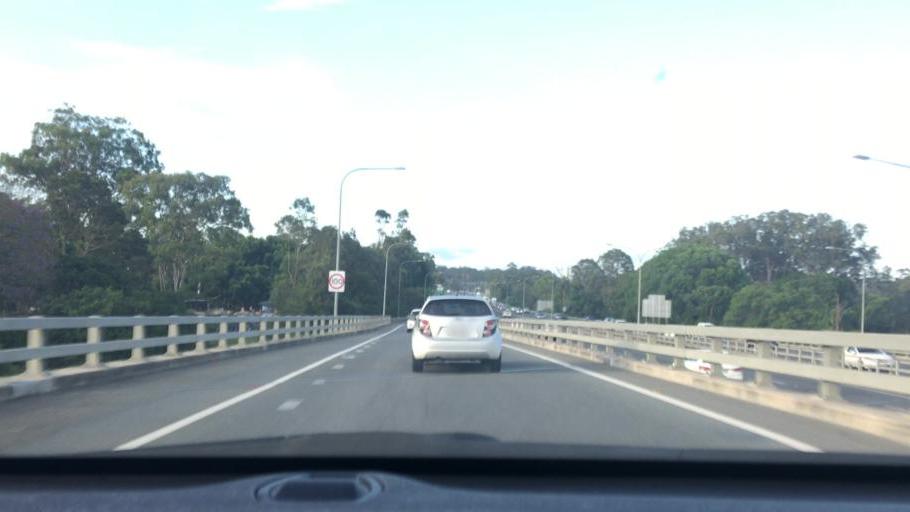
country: AU
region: Queensland
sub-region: Gold Coast
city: Nerang
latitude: -27.9918
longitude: 153.3401
